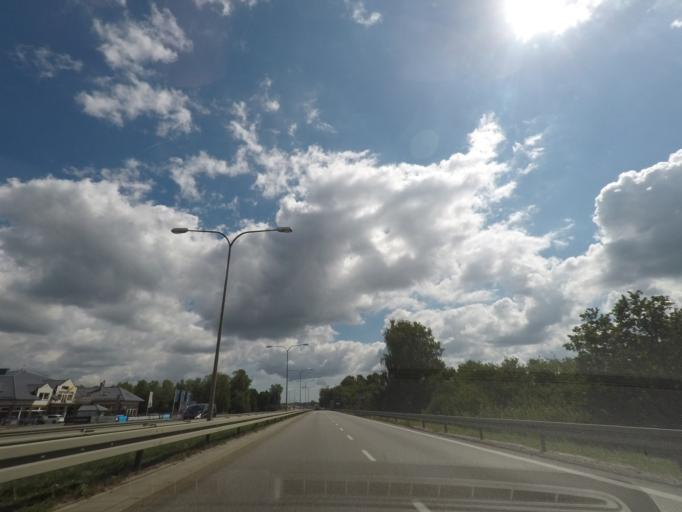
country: PL
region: Pomeranian Voivodeship
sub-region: Powiat wejherowski
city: Wejherowo
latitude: 54.6086
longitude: 18.2070
